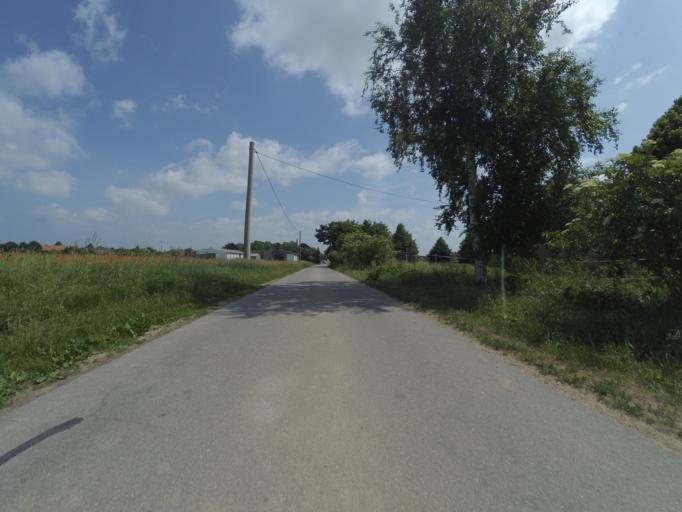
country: DE
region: Mecklenburg-Vorpommern
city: Lubz
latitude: 53.4044
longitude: 12.0056
